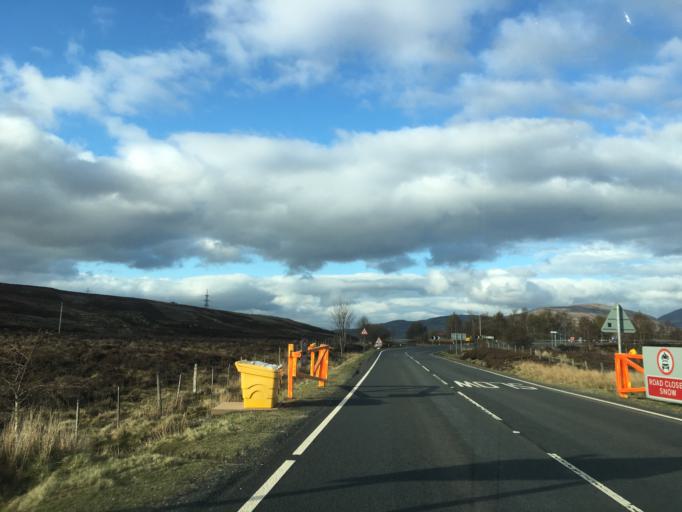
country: GB
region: Scotland
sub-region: Highland
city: Kingussie
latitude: 56.9425
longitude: -4.2397
